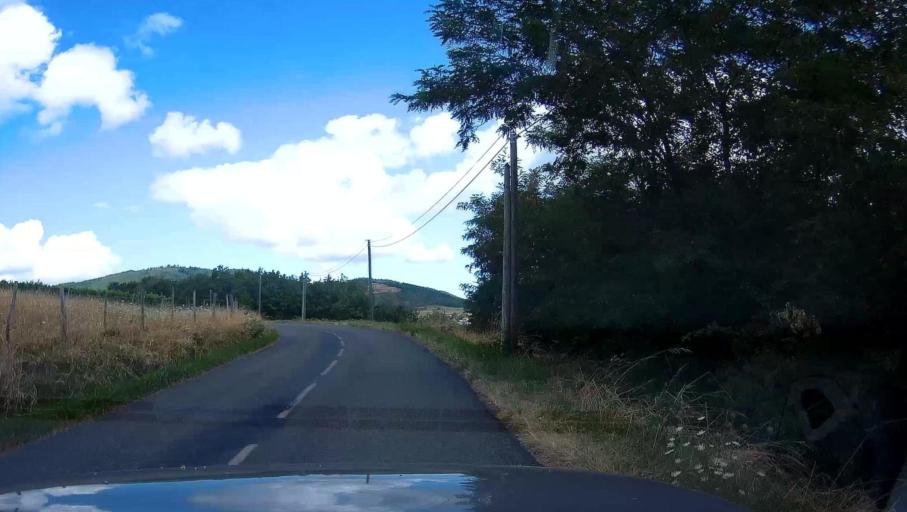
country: FR
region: Rhone-Alpes
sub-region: Departement du Rhone
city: Cogny
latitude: 45.9800
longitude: 4.5917
